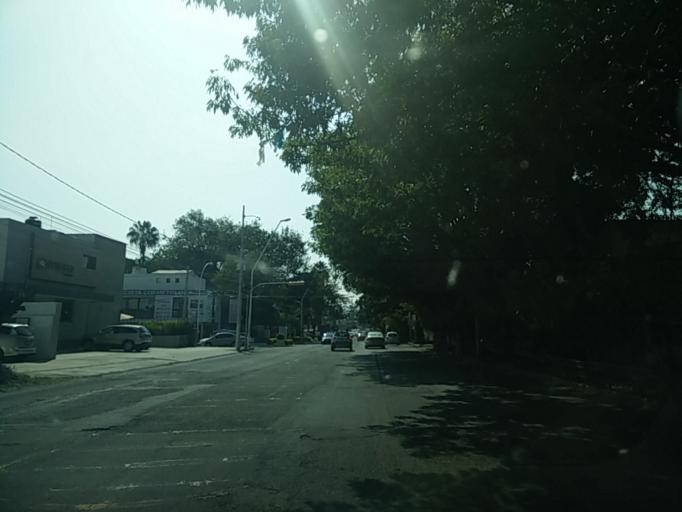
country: MX
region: Jalisco
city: Guadalajara
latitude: 20.6697
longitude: -103.3735
